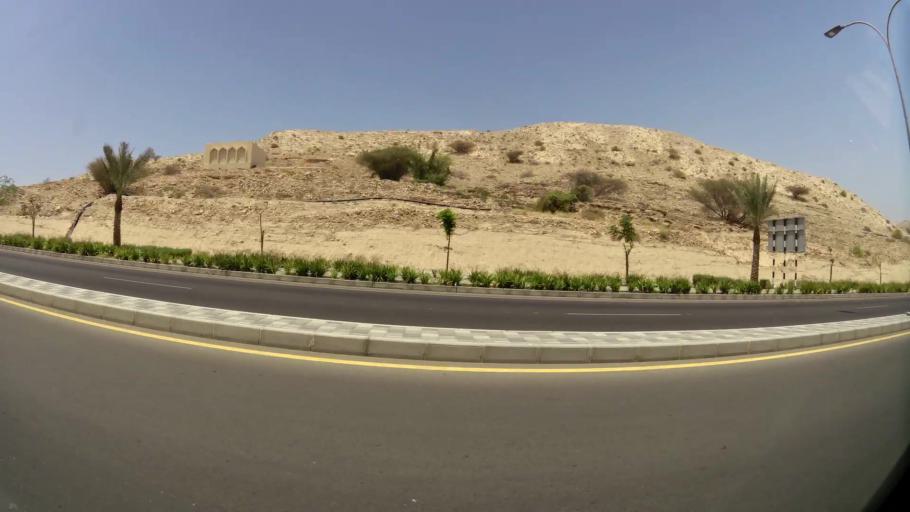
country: OM
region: Muhafazat Masqat
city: Muscat
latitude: 23.6244
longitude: 58.5047
